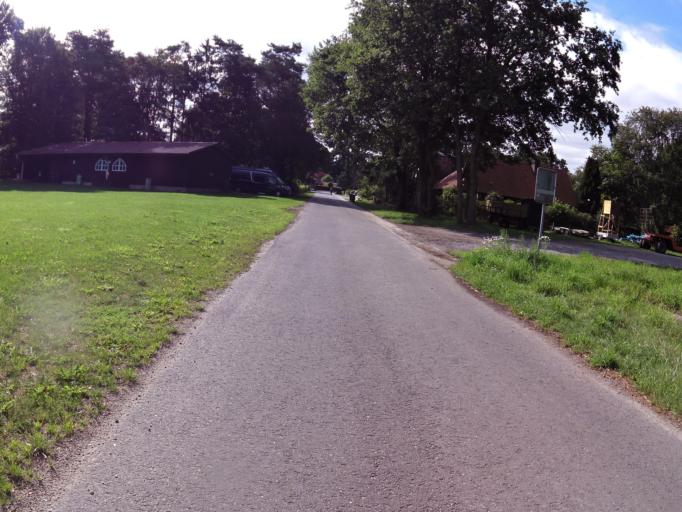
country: DE
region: Lower Saxony
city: Sandbostel
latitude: 53.4339
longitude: 9.1240
